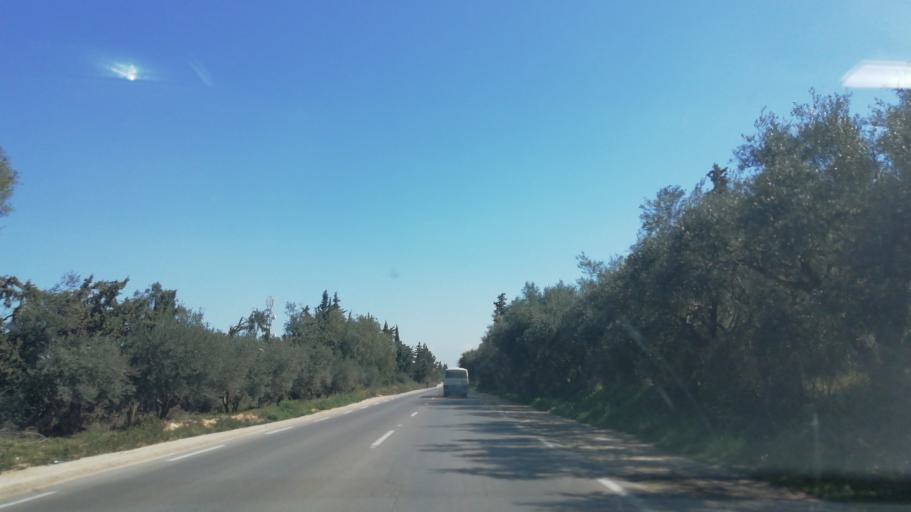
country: DZ
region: Mascara
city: Sig
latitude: 35.5662
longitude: -0.0763
